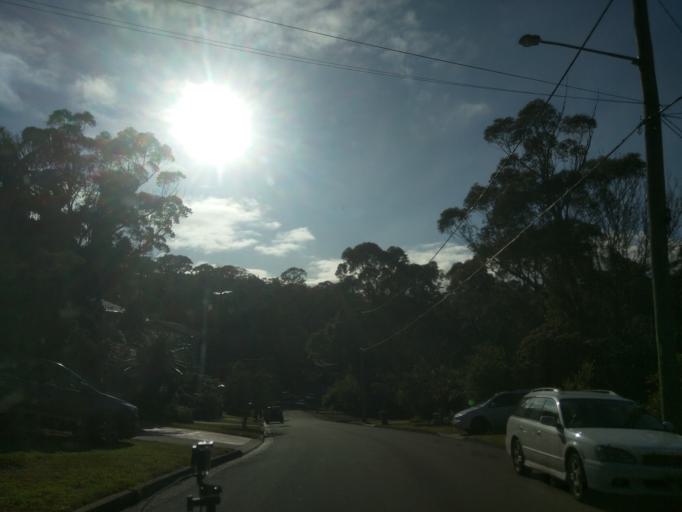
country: AU
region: New South Wales
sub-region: Hurstville
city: Lugarno
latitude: -33.9884
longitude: 151.0428
